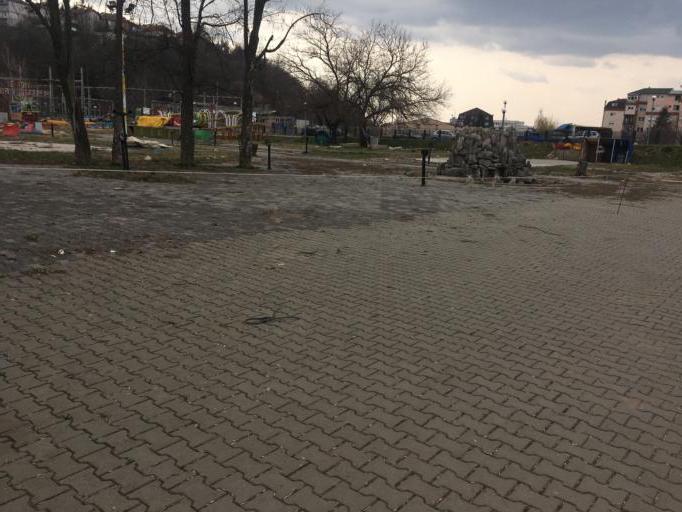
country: XK
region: Pristina
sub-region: Komuna e Prishtines
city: Pristina
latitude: 42.6657
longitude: 21.1781
